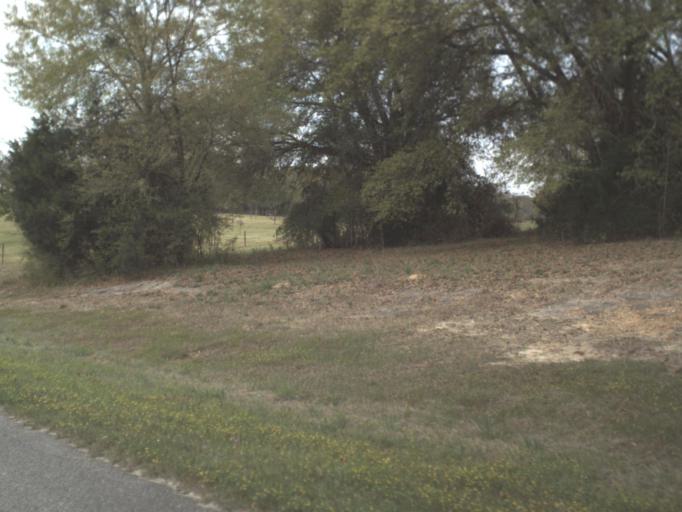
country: US
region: Florida
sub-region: Holmes County
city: Bonifay
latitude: 30.8853
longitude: -85.6592
